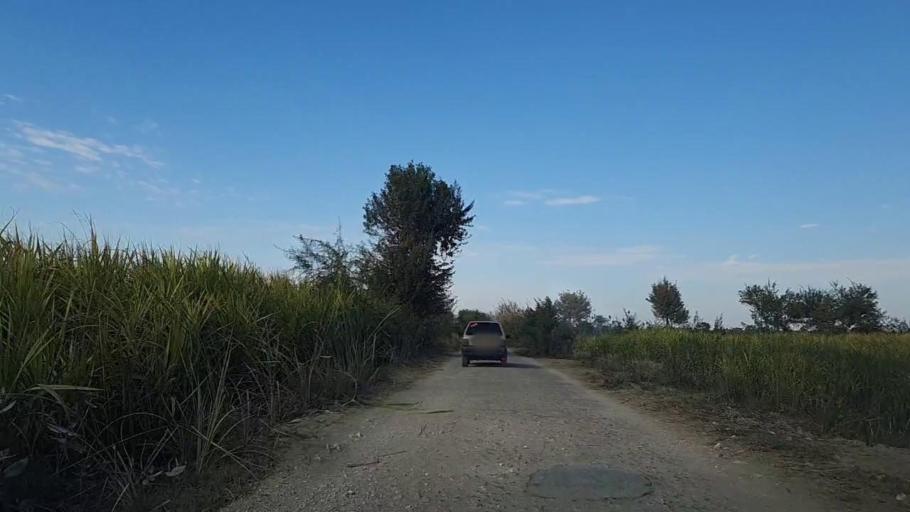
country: PK
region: Sindh
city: Khadro
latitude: 26.2811
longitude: 68.8200
